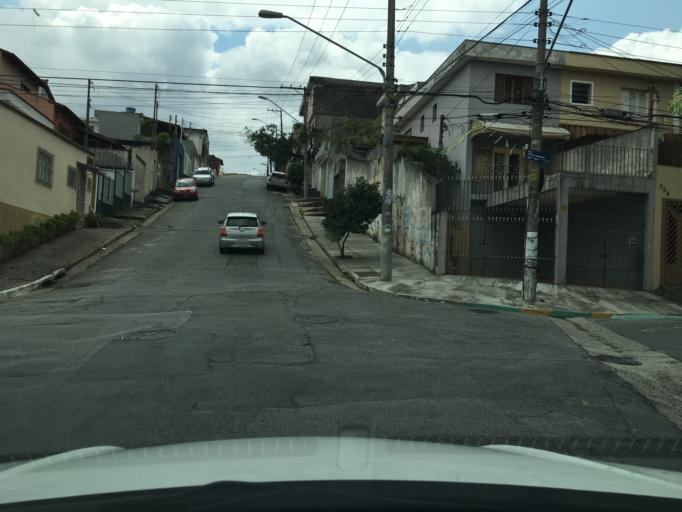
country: BR
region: Sao Paulo
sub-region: Sao Paulo
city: Sao Paulo
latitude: -23.4987
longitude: -46.6524
